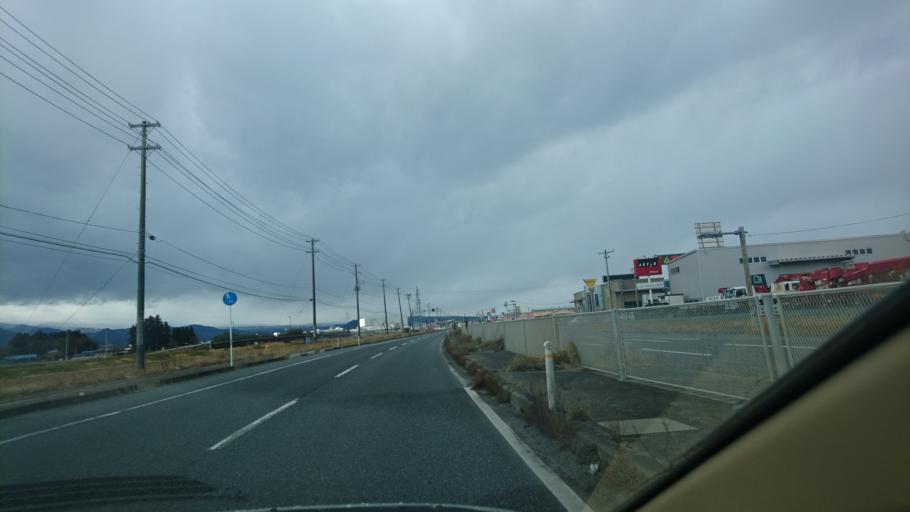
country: JP
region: Miyagi
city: Tomiya
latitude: 38.4349
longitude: 140.9125
